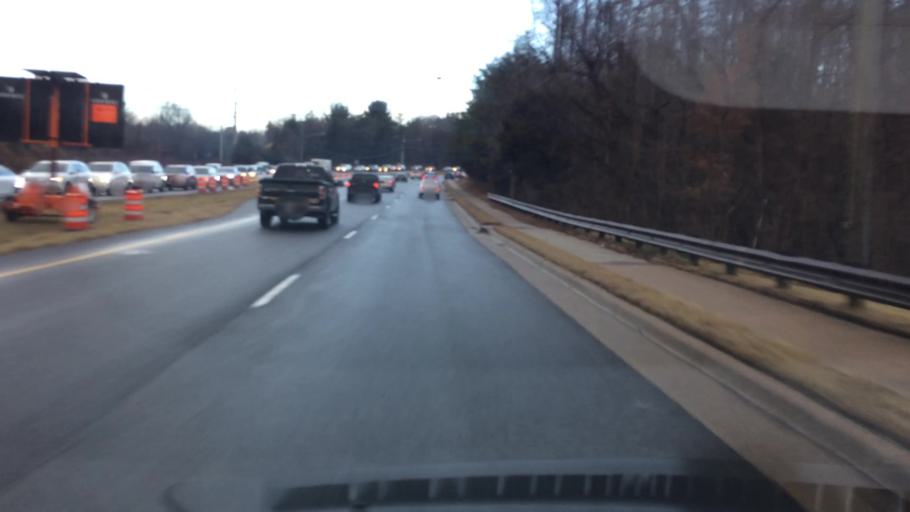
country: US
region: Virginia
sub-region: City of Fairfax
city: Fairfax
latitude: 38.8317
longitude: -77.3324
